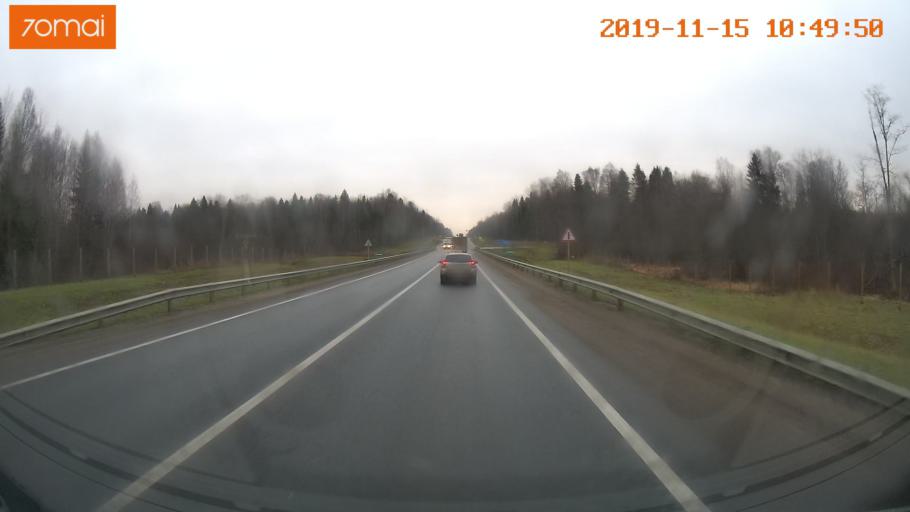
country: RU
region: Vologda
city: Sheksna
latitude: 59.1881
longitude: 38.6687
